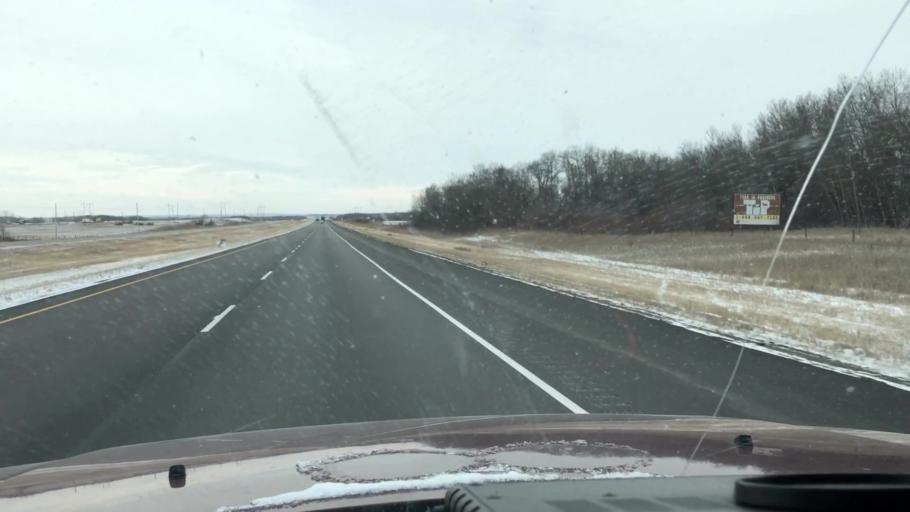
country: CA
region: Saskatchewan
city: Saskatoon
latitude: 51.9010
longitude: -106.5218
